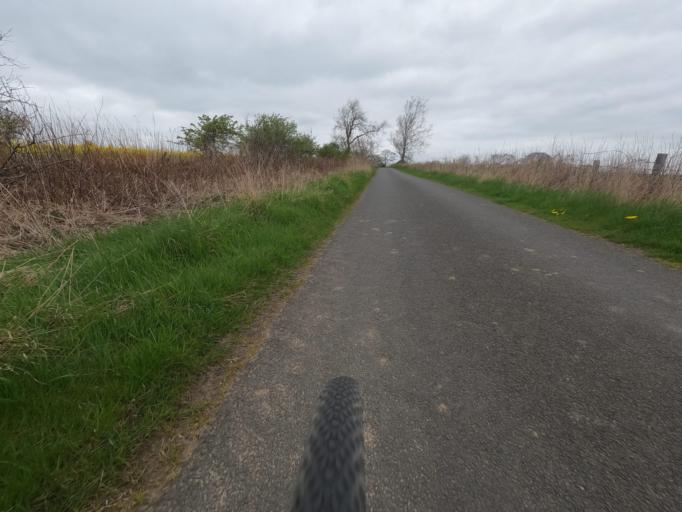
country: GB
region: England
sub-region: Northumberland
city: Horsley
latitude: 55.0582
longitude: -1.8443
